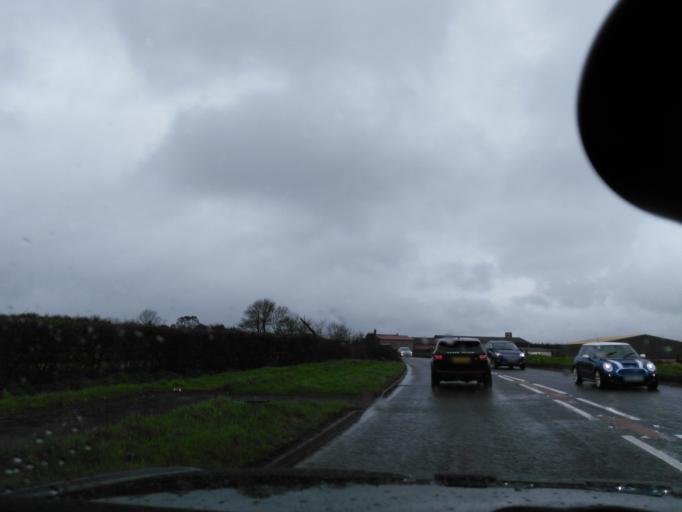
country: GB
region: England
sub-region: Somerset
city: Shepton Mallet
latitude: 51.1713
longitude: -2.5341
